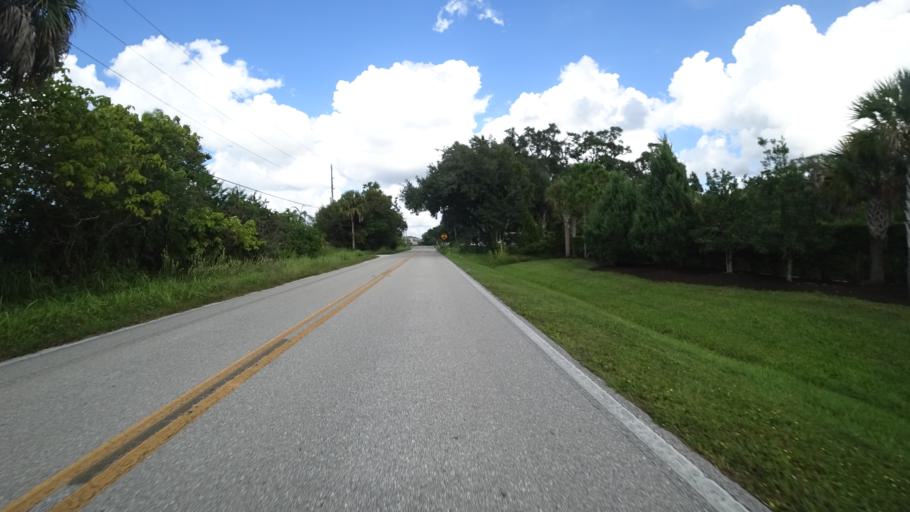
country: US
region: Florida
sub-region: Manatee County
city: Samoset
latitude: 27.4269
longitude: -82.5177
